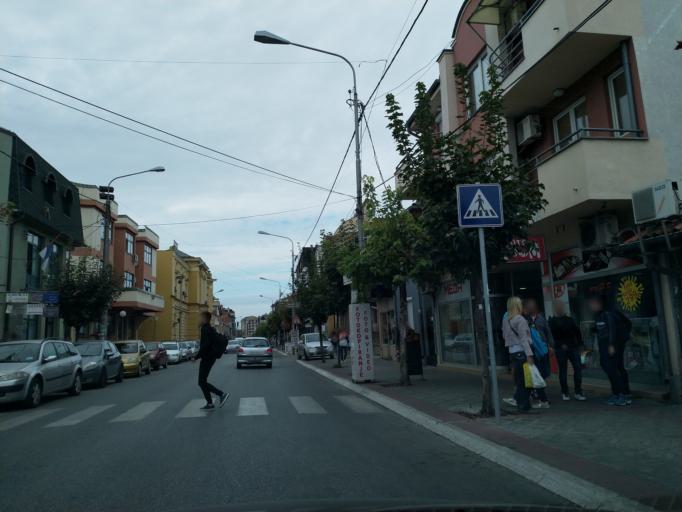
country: RS
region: Central Serbia
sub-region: Pomoravski Okrug
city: Jagodina
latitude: 43.9752
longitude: 21.2643
